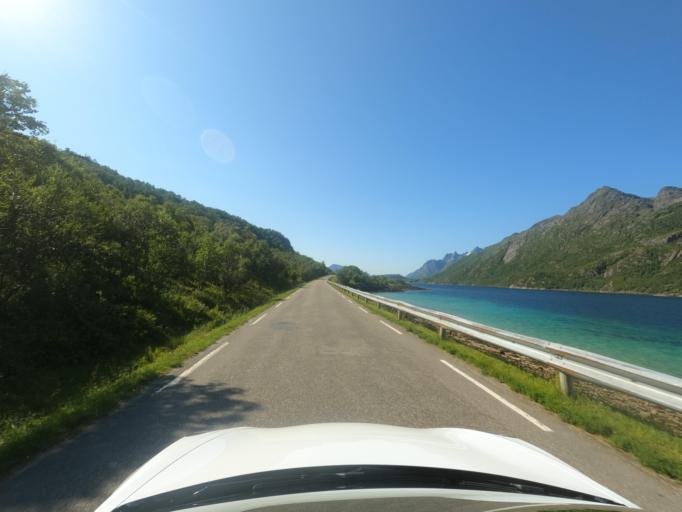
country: NO
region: Nordland
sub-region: Hadsel
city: Stokmarknes
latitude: 68.3884
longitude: 15.0972
